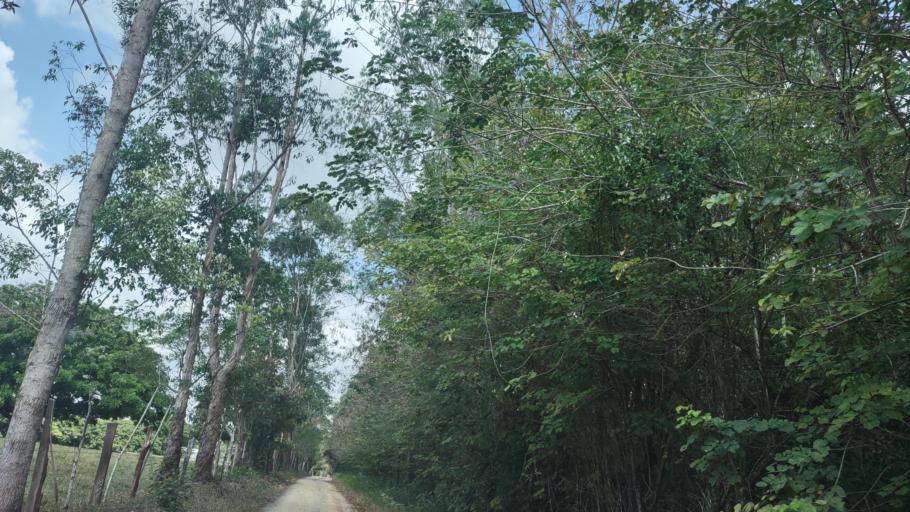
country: MX
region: Veracruz
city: Las Choapas
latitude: 17.9454
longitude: -94.1008
